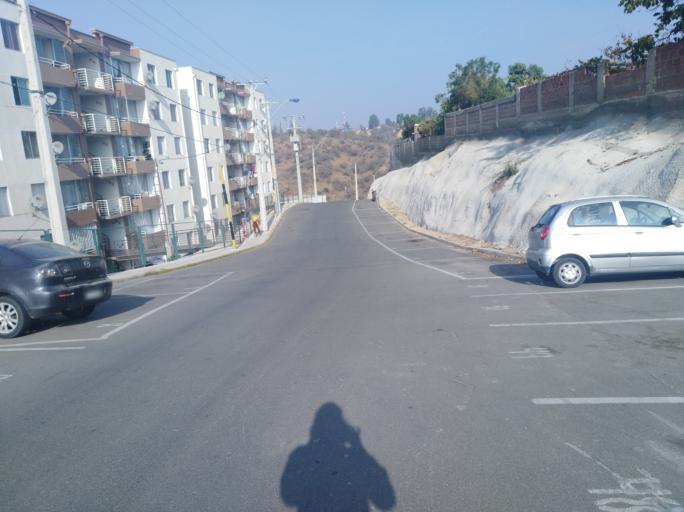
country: CL
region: Valparaiso
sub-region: Provincia de Marga Marga
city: Quilpue
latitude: -33.0656
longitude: -71.4354
